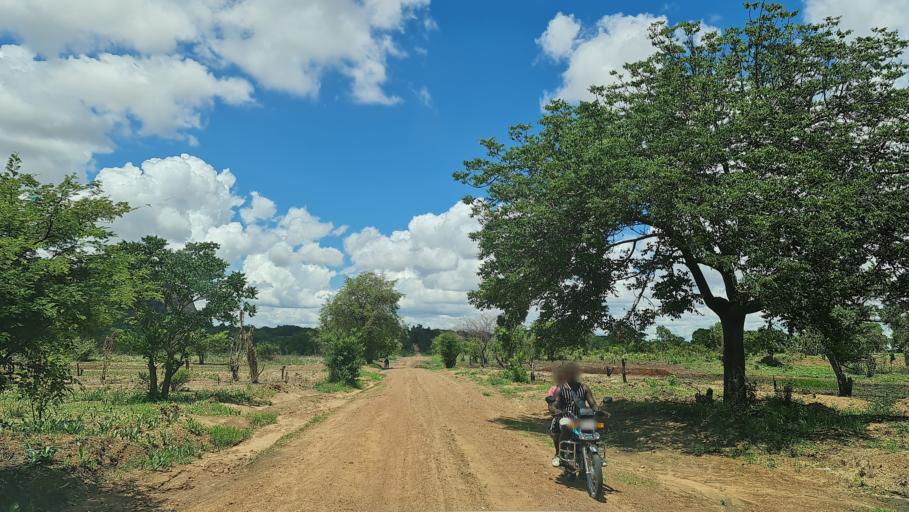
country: MZ
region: Cabo Delgado
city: Montepuez
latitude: -13.8451
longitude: 39.5537
